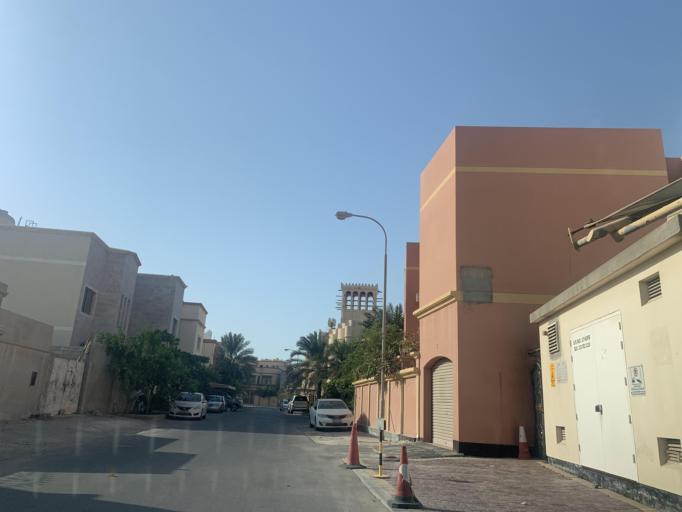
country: BH
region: Muharraq
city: Al Muharraq
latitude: 26.2825
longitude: 50.6296
